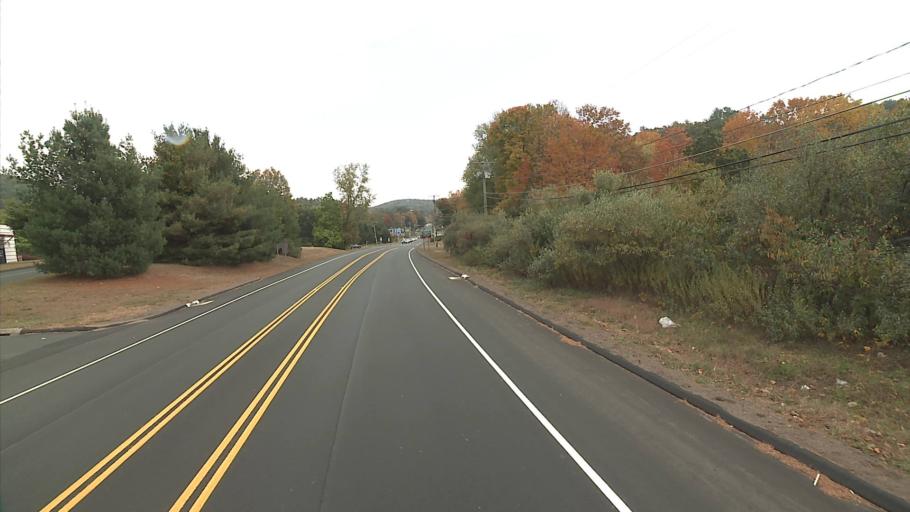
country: US
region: Connecticut
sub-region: Litchfield County
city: Thomaston
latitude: 41.6560
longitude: -73.0912
